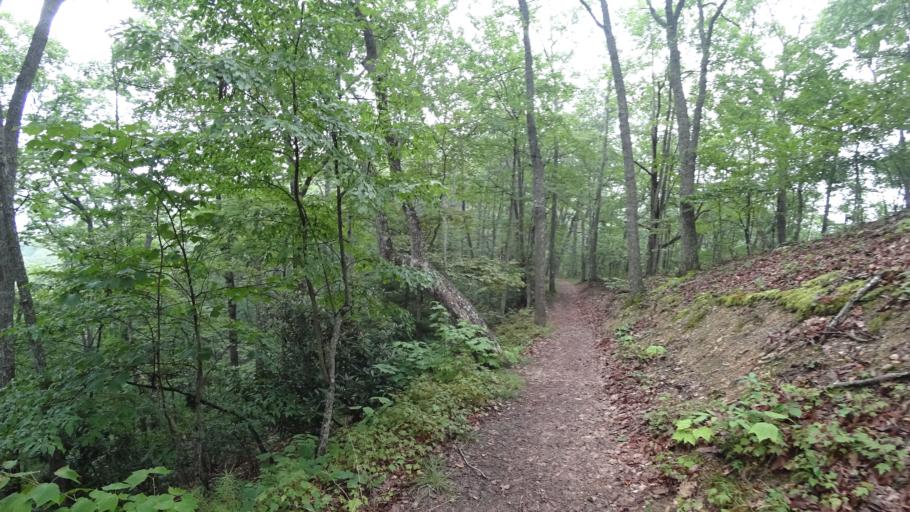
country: US
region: Virginia
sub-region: Smyth County
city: Marion
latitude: 36.8845
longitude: -81.5178
